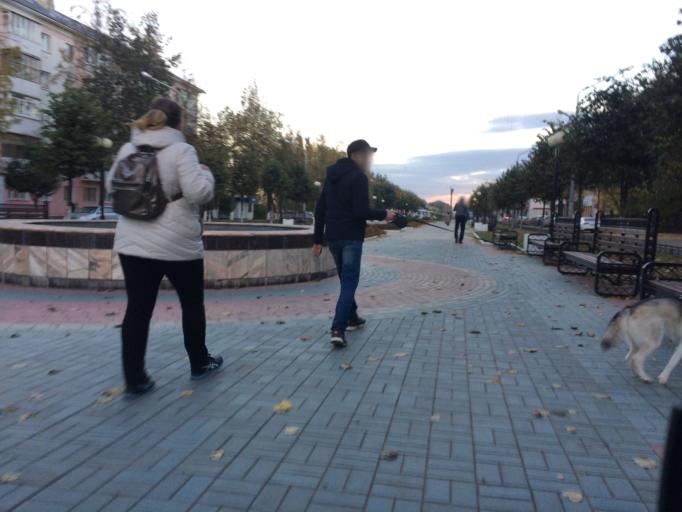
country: RU
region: Mariy-El
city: Yoshkar-Ola
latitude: 56.6388
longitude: 47.8788
